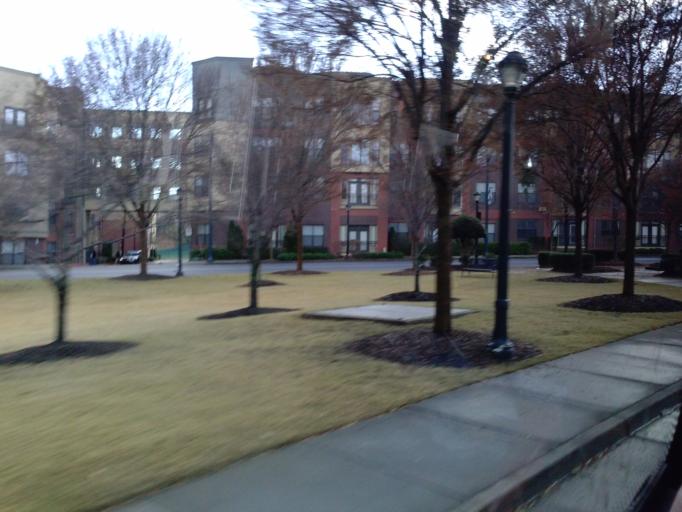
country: US
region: Georgia
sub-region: Fulton County
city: Atlanta
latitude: 33.7900
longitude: -84.4021
